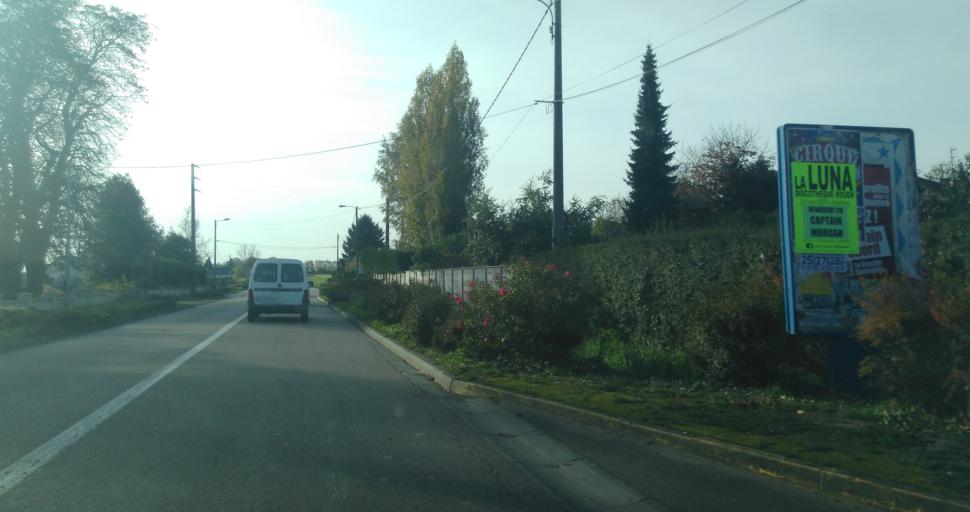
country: FR
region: Haute-Normandie
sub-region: Departement de l'Eure
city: Bourg-Achard
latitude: 49.3598
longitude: 0.8492
